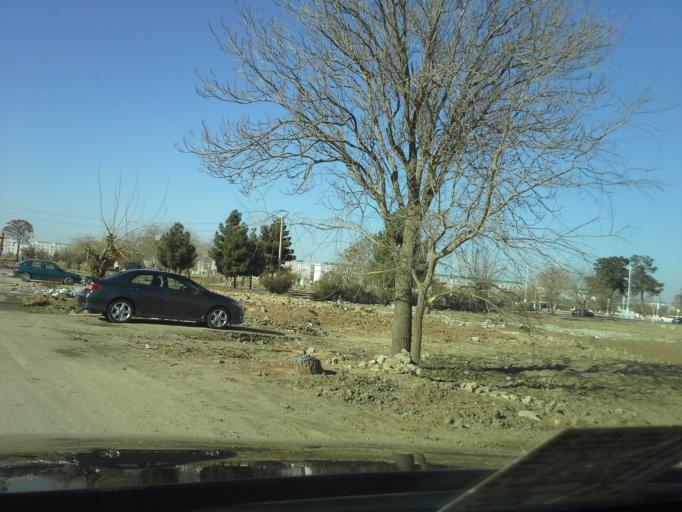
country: TM
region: Ahal
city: Ashgabat
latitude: 37.9597
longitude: 58.3354
